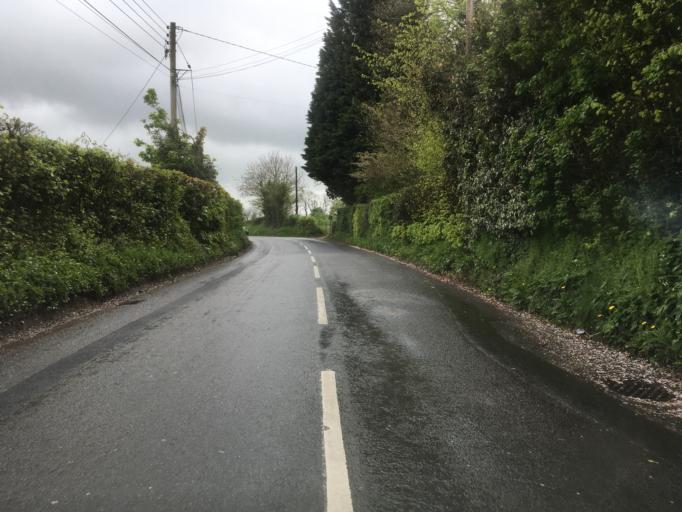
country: GB
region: England
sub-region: Bath and North East Somerset
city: Compton Martin
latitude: 51.3108
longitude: -2.6497
